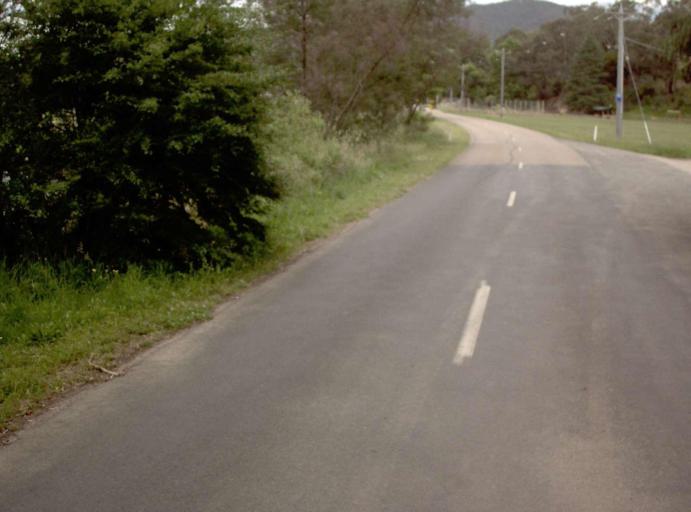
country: AU
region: Victoria
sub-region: East Gippsland
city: Bairnsdale
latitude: -37.4553
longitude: 147.2513
